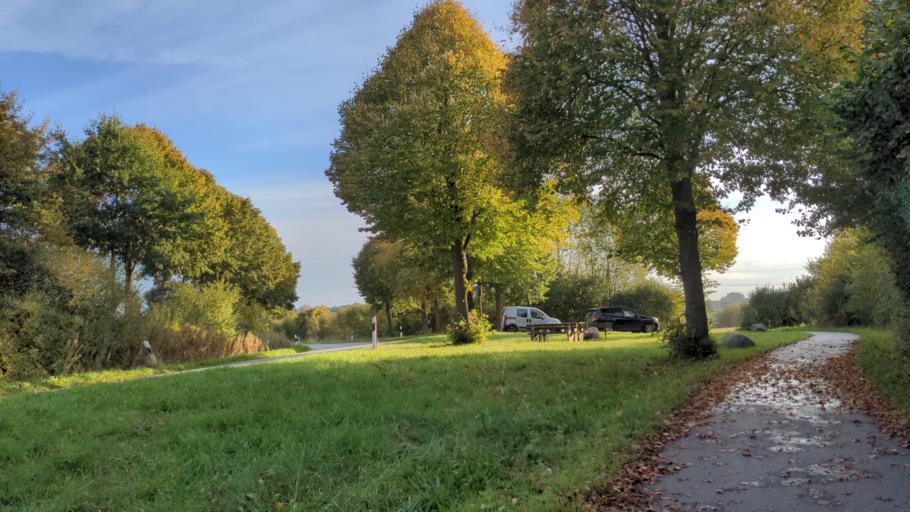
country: DE
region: Schleswig-Holstein
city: Kabelhorst
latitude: 54.2117
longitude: 10.9194
